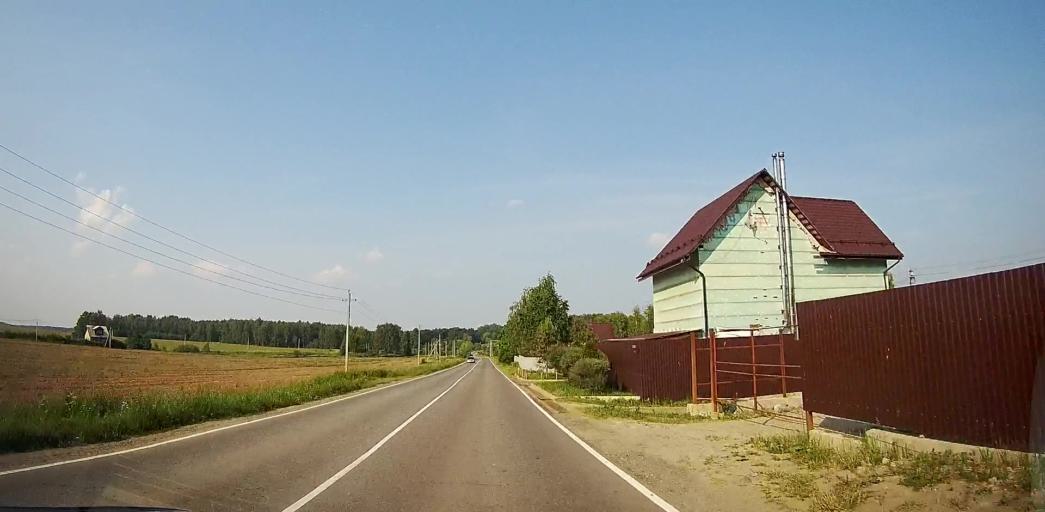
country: RU
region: Moskovskaya
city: Yakovlevskoye
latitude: 55.4275
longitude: 37.9611
